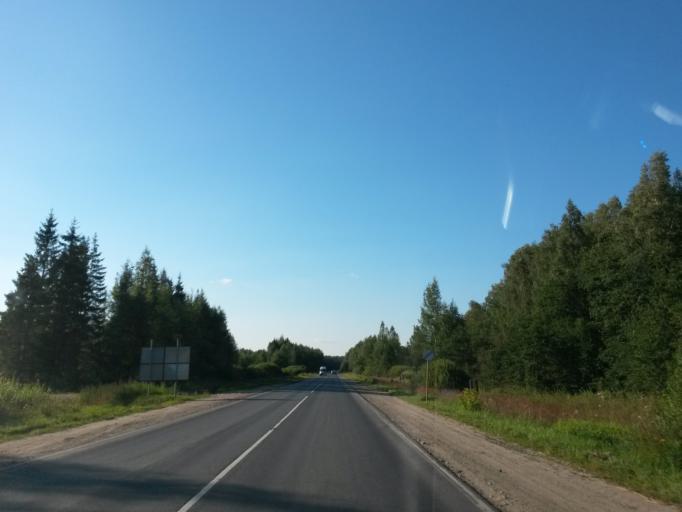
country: RU
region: Ivanovo
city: Pistsovo
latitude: 57.0949
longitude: 40.6603
